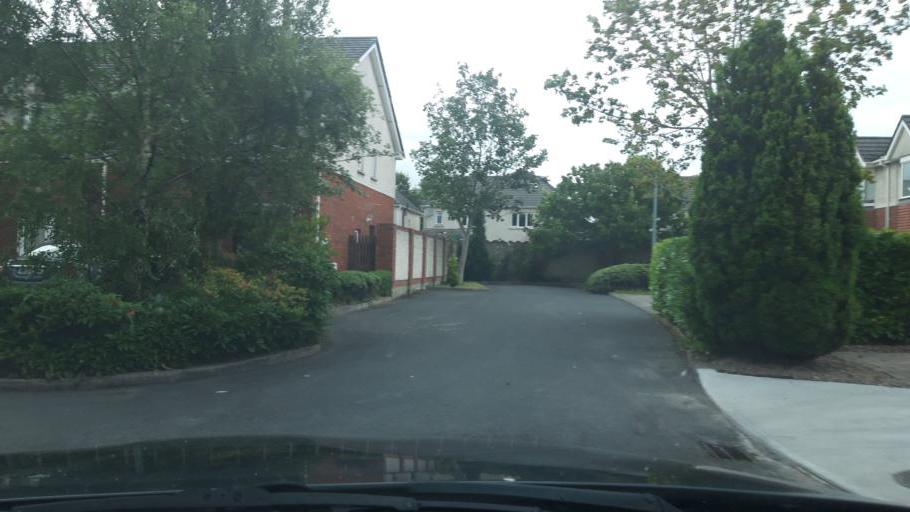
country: IE
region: Leinster
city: Hartstown
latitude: 53.4022
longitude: -6.4248
